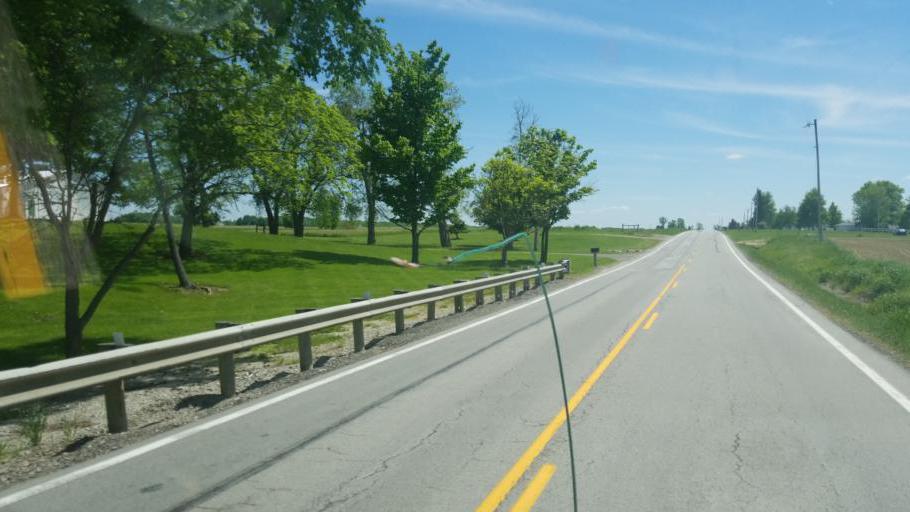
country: US
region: Ohio
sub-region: Huron County
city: Willard
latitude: 41.1141
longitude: -82.7196
